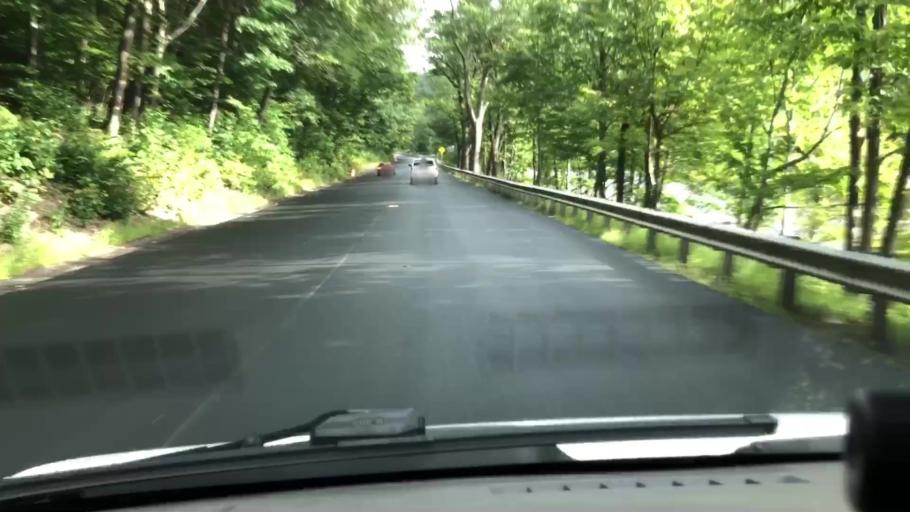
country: US
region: Massachusetts
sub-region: Franklin County
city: Charlemont
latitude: 42.6239
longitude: -72.8501
